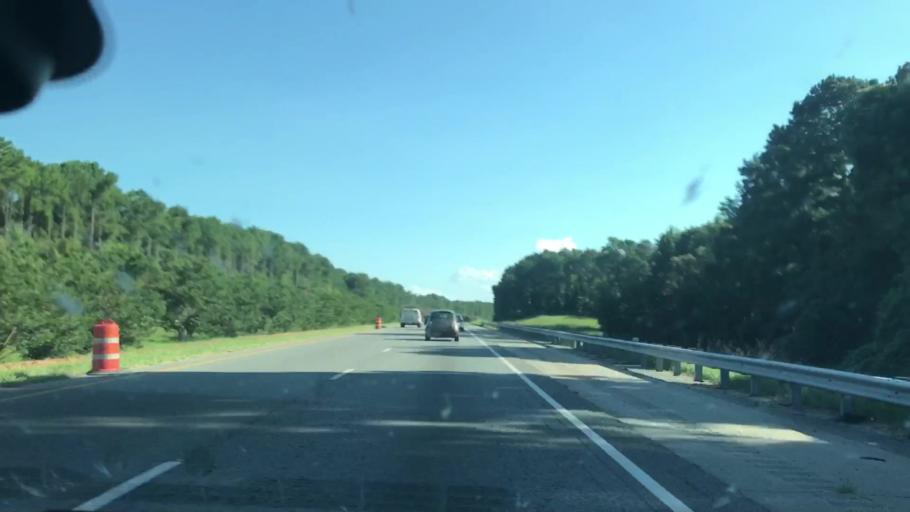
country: US
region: Georgia
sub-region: Harris County
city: Hamilton
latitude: 32.7887
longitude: -85.0207
